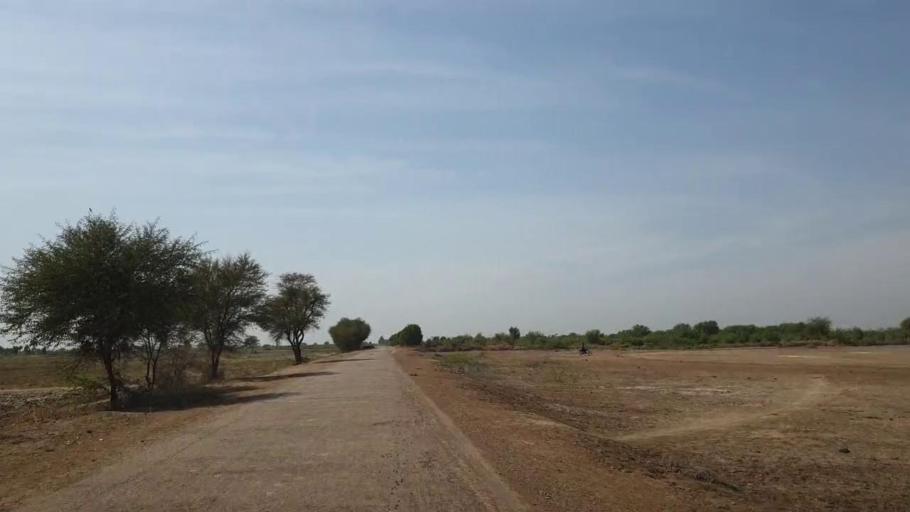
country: PK
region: Sindh
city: Kunri
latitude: 25.2124
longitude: 69.5414
